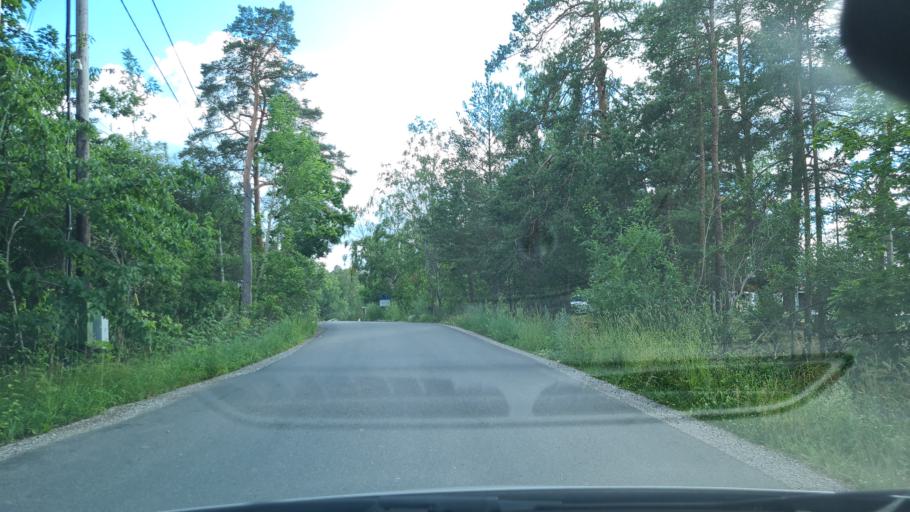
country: SE
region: Stockholm
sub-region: Vaxholms Kommun
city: Vaxholm
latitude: 59.4090
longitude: 18.3700
